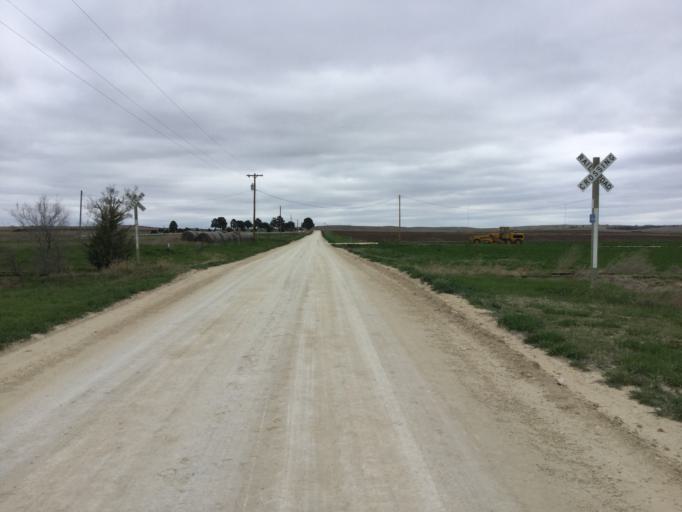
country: US
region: Kansas
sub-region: Osborne County
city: Osborne
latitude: 39.4447
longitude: -98.7129
